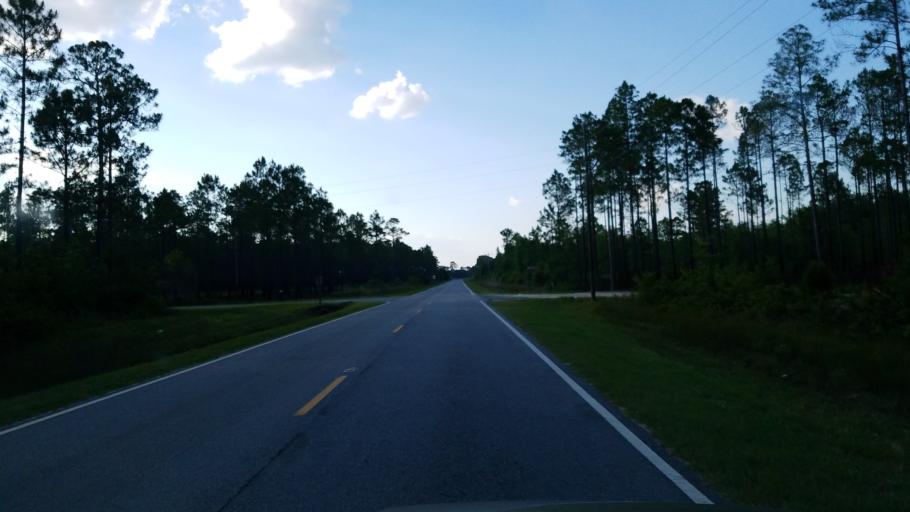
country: US
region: Georgia
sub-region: Lanier County
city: Lakeland
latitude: 31.1226
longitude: -83.0841
